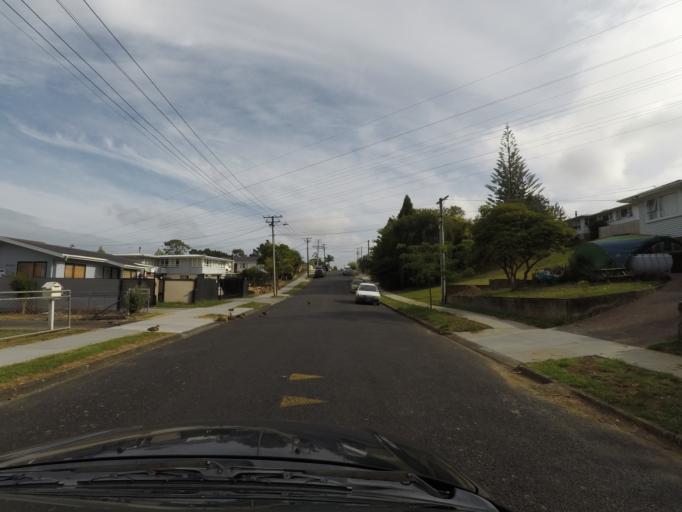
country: NZ
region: Auckland
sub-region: Auckland
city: Rosebank
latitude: -36.8973
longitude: 174.6711
